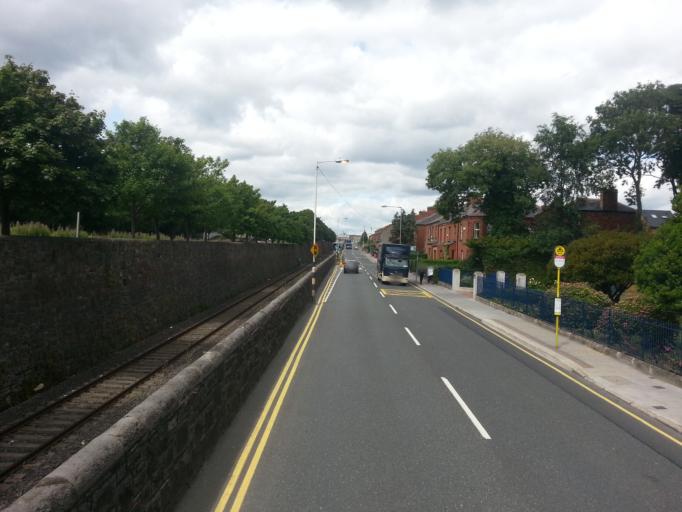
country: IE
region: Leinster
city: Drumcondra
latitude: 53.3629
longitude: -6.2646
